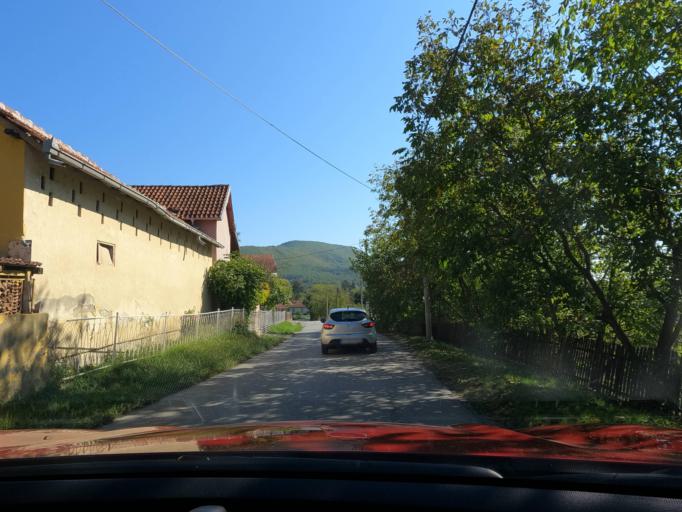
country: RS
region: Central Serbia
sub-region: Raski Okrug
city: Kraljevo
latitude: 43.7509
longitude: 20.7058
